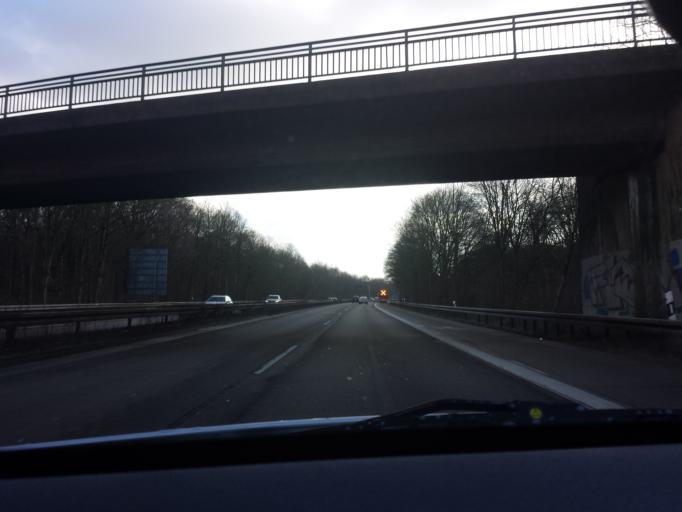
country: DE
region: North Rhine-Westphalia
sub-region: Regierungsbezirk Dusseldorf
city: Erkrath
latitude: 51.1818
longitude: 6.8790
